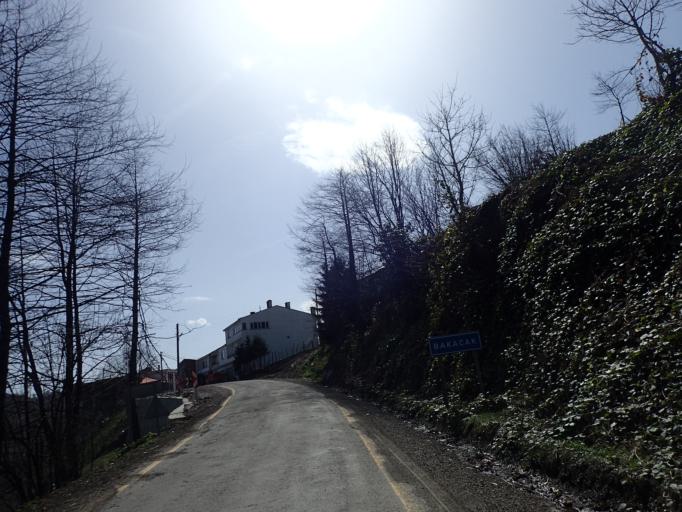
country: TR
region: Ordu
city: Kabaduz
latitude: 40.8219
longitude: 37.9038
